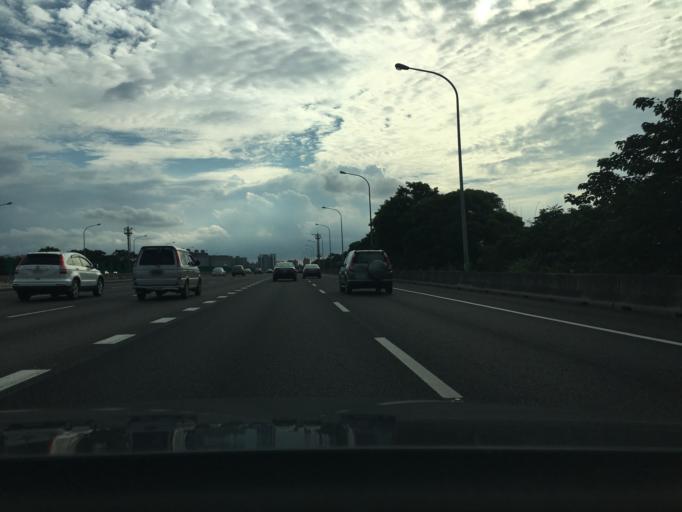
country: TW
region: Taiwan
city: Taoyuan City
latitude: 24.9758
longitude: 121.2229
